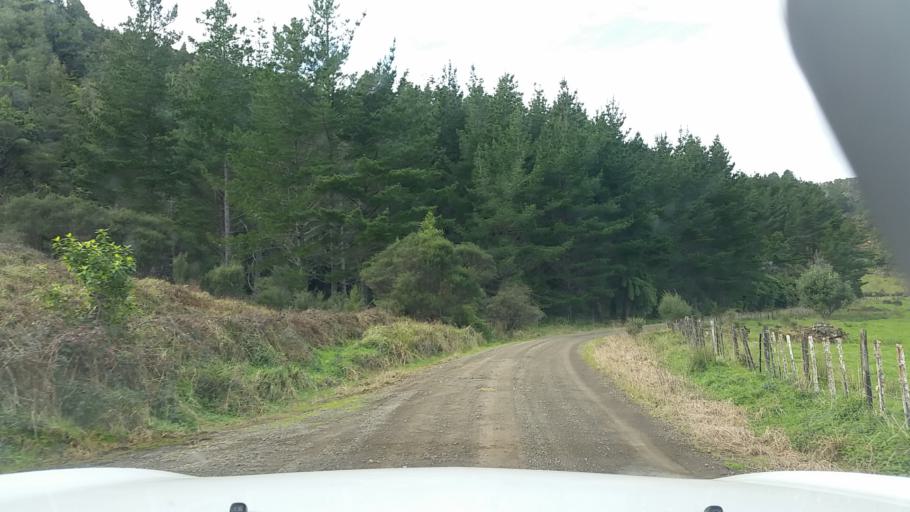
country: NZ
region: Taranaki
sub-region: New Plymouth District
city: Waitara
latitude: -38.8188
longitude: 174.6049
